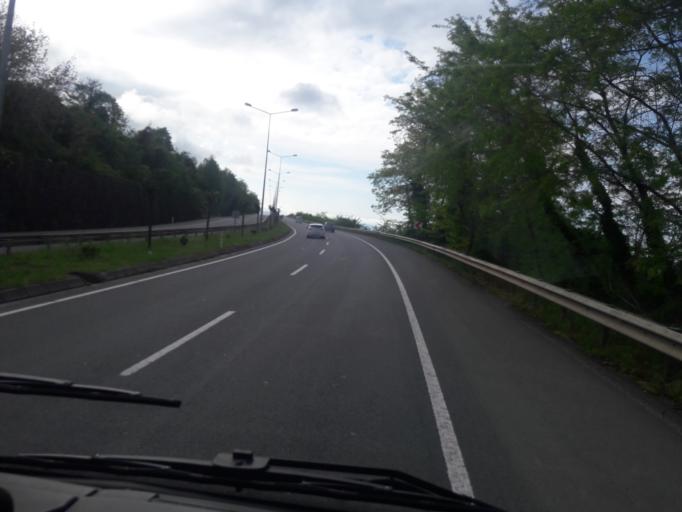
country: TR
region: Giresun
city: Piraziz
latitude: 40.9612
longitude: 38.1038
